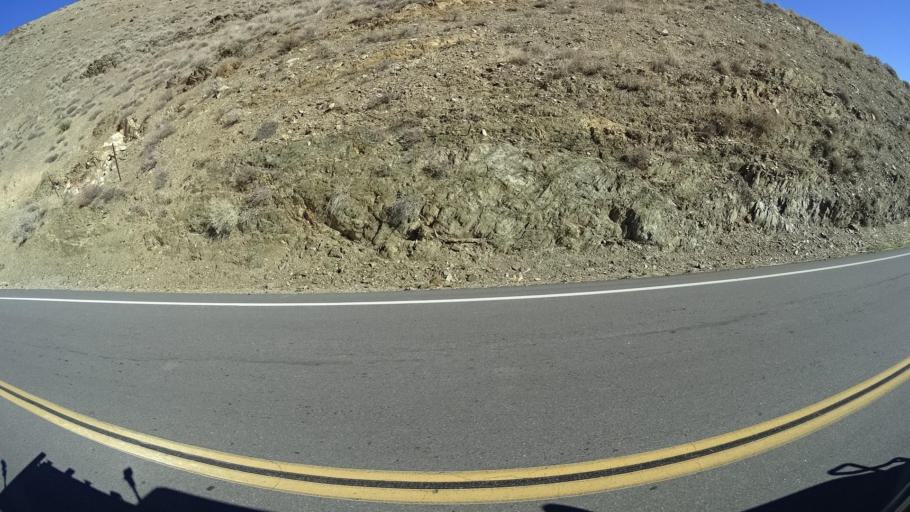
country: US
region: California
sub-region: Kern County
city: Wofford Heights
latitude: 35.6841
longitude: -118.4241
